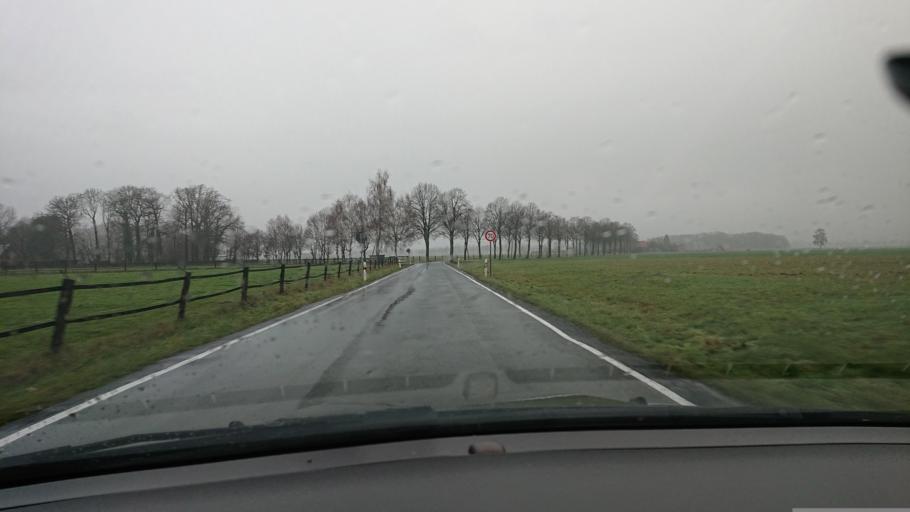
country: DE
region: North Rhine-Westphalia
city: Oelde
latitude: 51.8617
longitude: 8.2019
